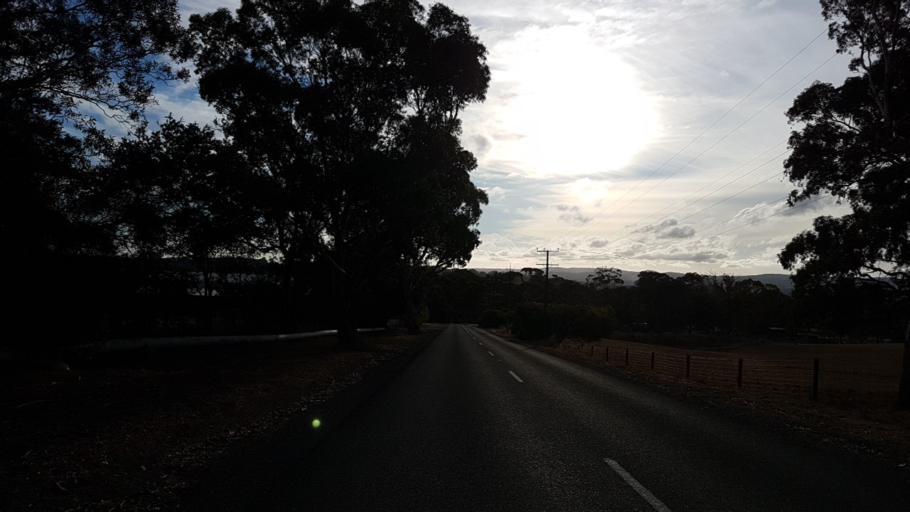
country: AU
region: South Australia
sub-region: Mount Barker
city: Nairne
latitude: -34.9930
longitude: 138.9077
